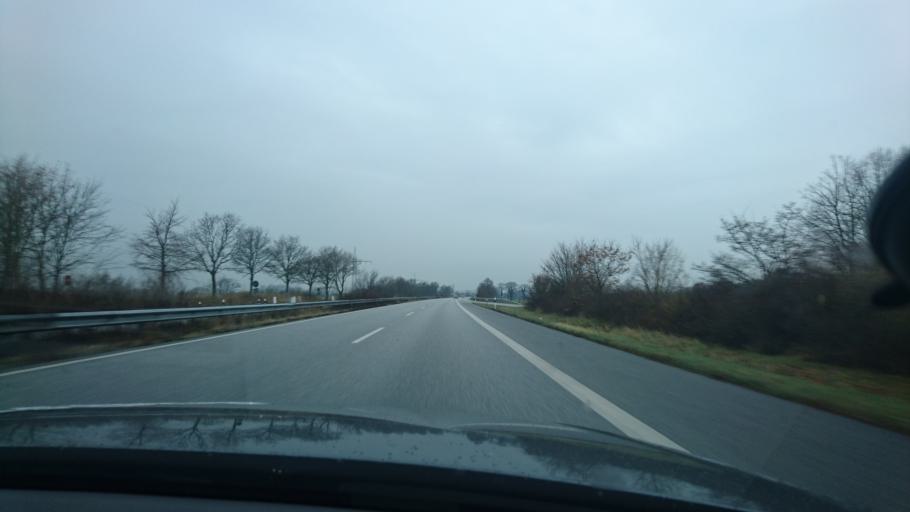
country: DE
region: Schleswig-Holstein
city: Lensahn
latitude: 54.2404
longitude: 10.8913
